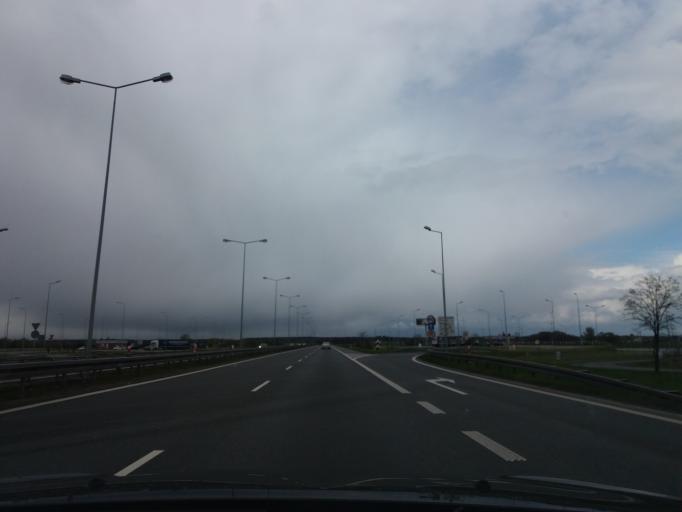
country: PL
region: Opole Voivodeship
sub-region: Powiat opolski
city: Proszkow
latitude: 50.5679
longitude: 17.8630
